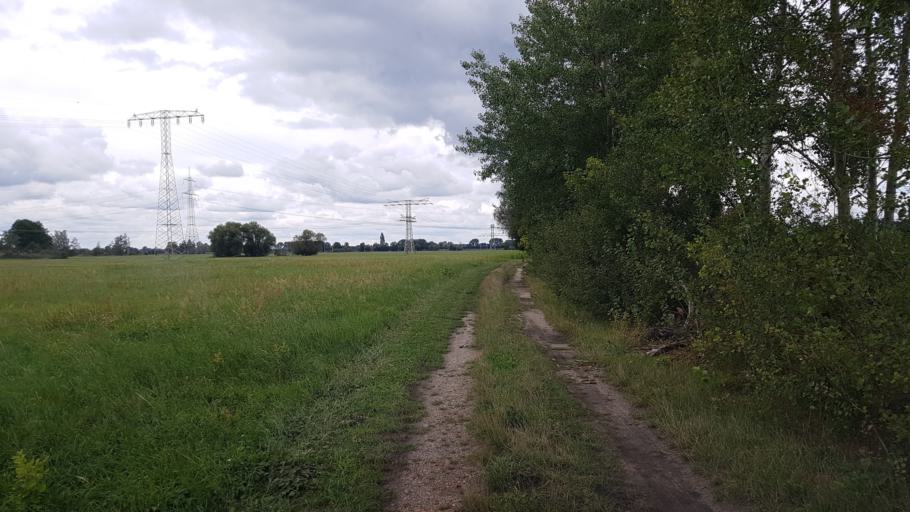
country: DE
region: Brandenburg
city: Doberlug-Kirchhain
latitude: 51.6454
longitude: 13.5868
